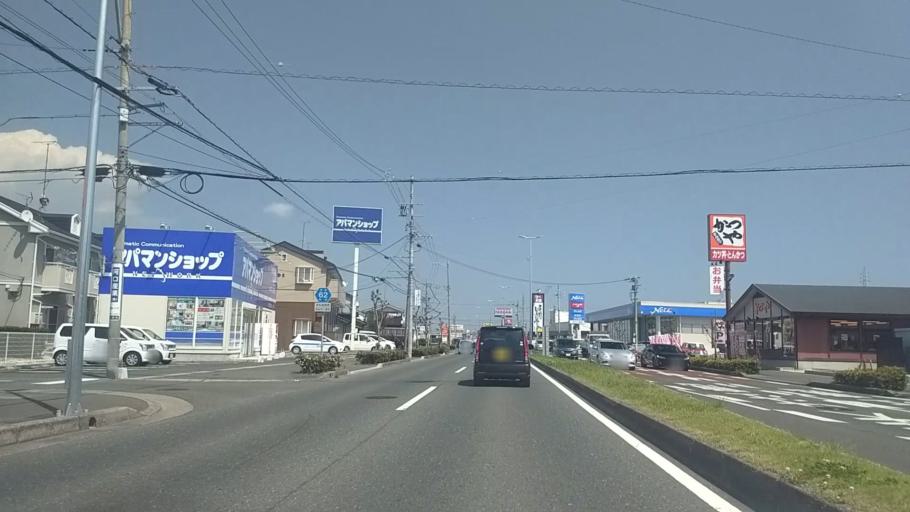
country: JP
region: Shizuoka
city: Hamamatsu
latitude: 34.6979
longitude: 137.6801
